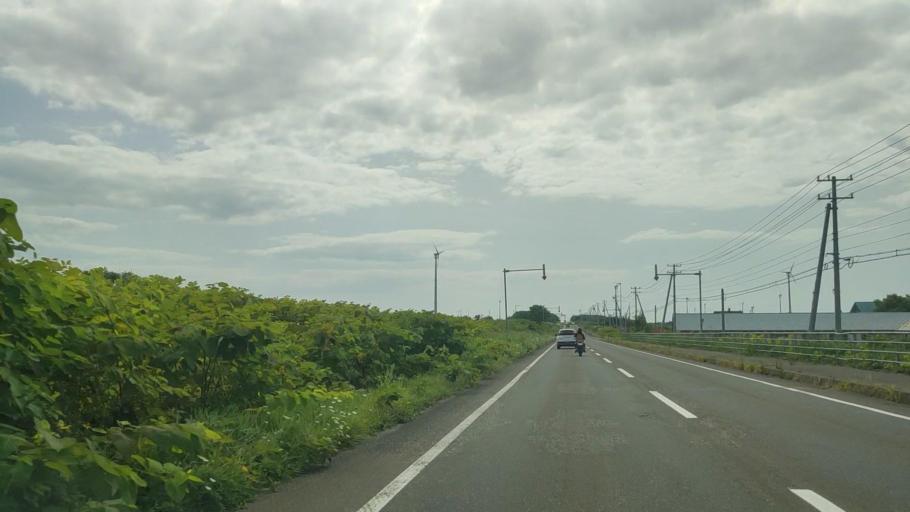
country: JP
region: Hokkaido
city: Rumoi
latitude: 44.4020
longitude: 141.7253
